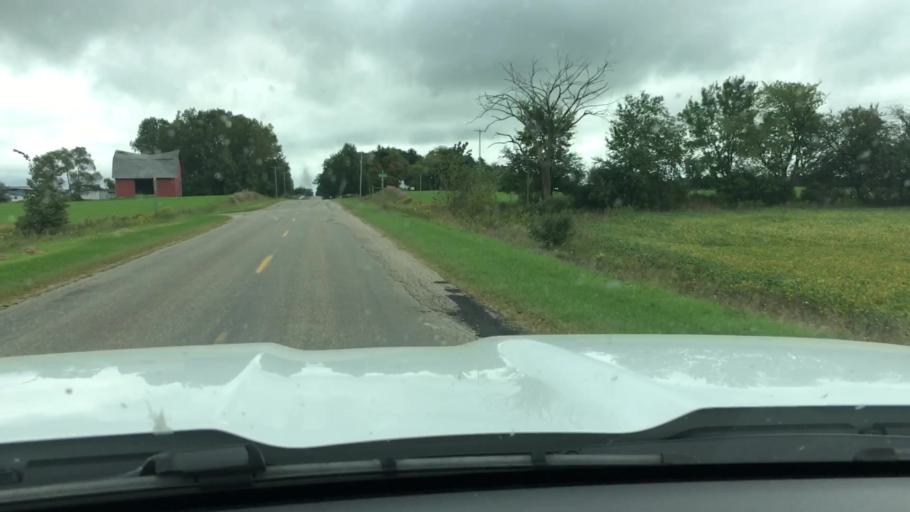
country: US
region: Michigan
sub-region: Montcalm County
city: Carson City
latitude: 43.2485
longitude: -84.7683
